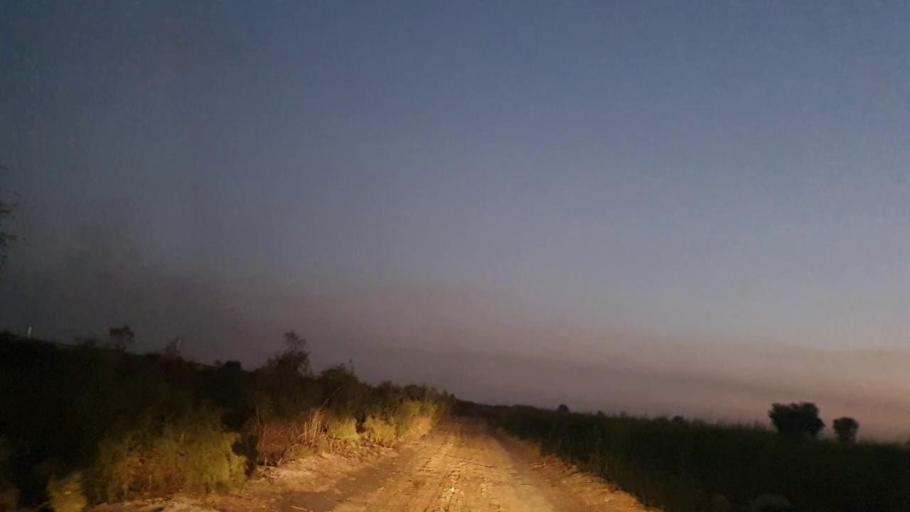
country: PK
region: Sindh
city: Nawabshah
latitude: 26.3286
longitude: 68.3760
